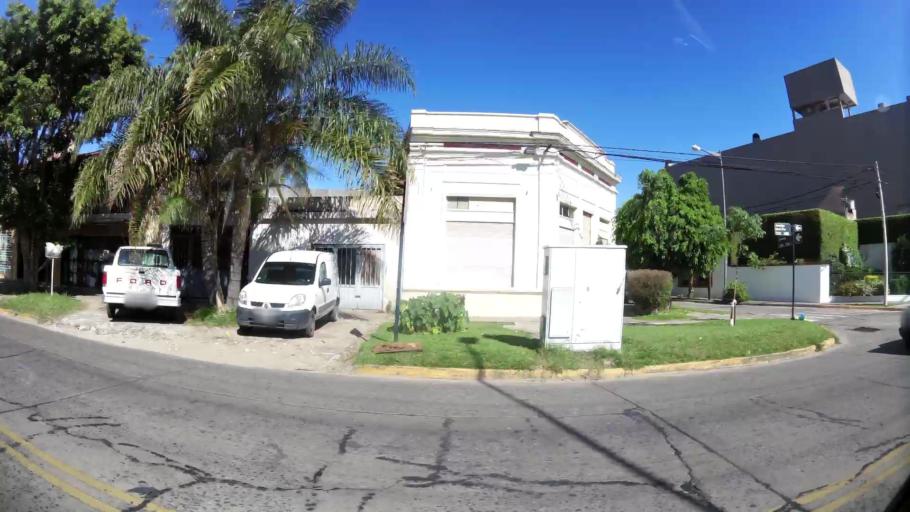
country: AR
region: Santa Fe
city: Santa Fe de la Vera Cruz
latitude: -31.6245
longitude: -60.6888
